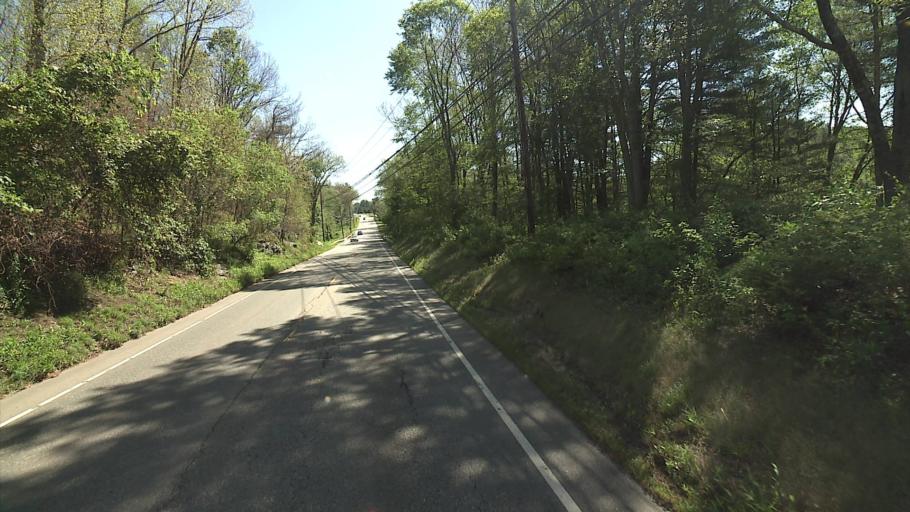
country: US
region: Connecticut
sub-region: New London County
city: Colchester
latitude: 41.5670
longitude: -72.3455
